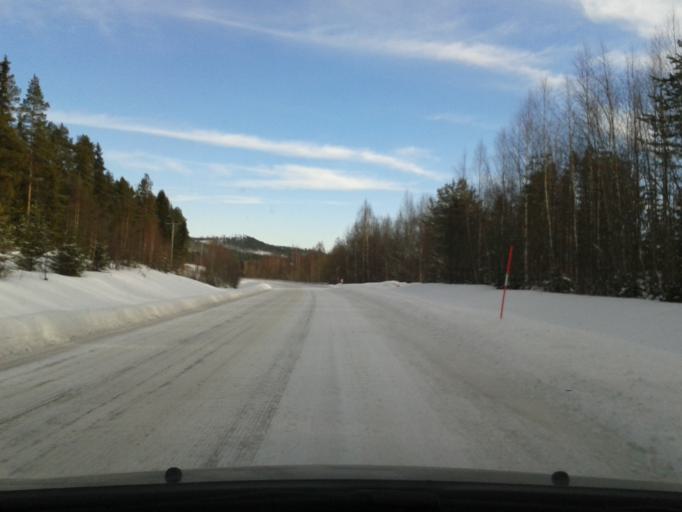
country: SE
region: Vaesterbotten
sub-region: Asele Kommun
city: Asele
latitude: 64.3232
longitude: 17.0764
